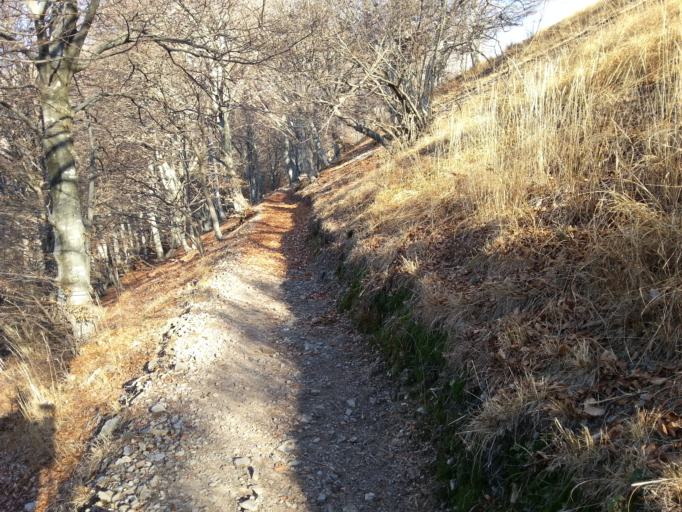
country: CH
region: Ticino
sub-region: Lugano District
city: Cadro
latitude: 46.0234
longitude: 9.0101
